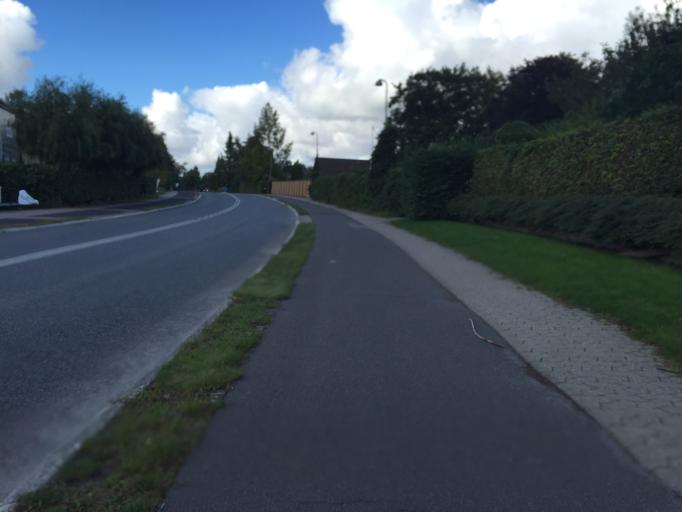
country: DK
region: Capital Region
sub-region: Fureso Kommune
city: Vaerlose
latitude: 55.7732
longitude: 12.3862
